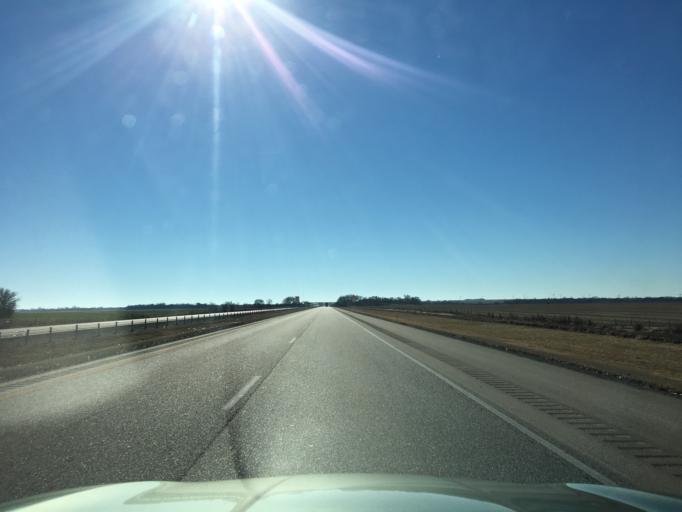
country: US
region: Oklahoma
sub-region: Kay County
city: Blackwell
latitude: 36.9212
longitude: -97.3505
